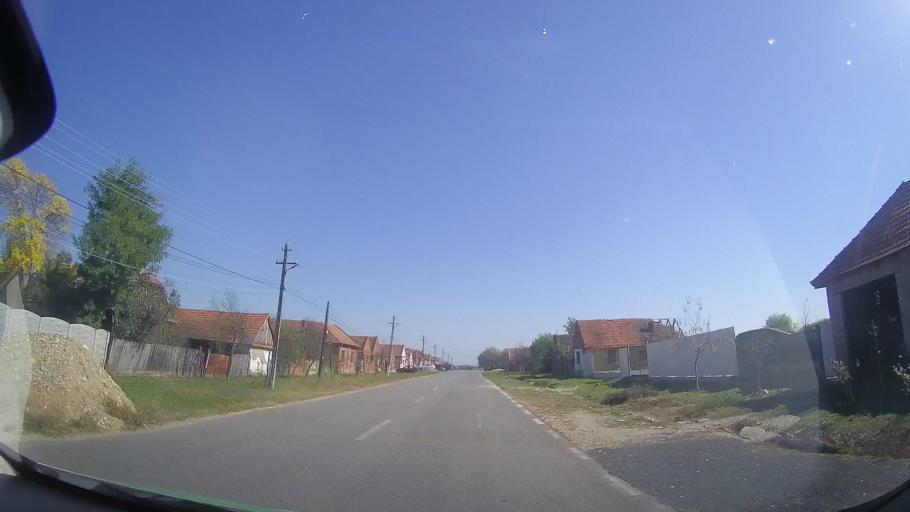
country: RO
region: Timis
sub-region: Comuna Bethausen
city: Bethausen
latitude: 45.7939
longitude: 21.9680
